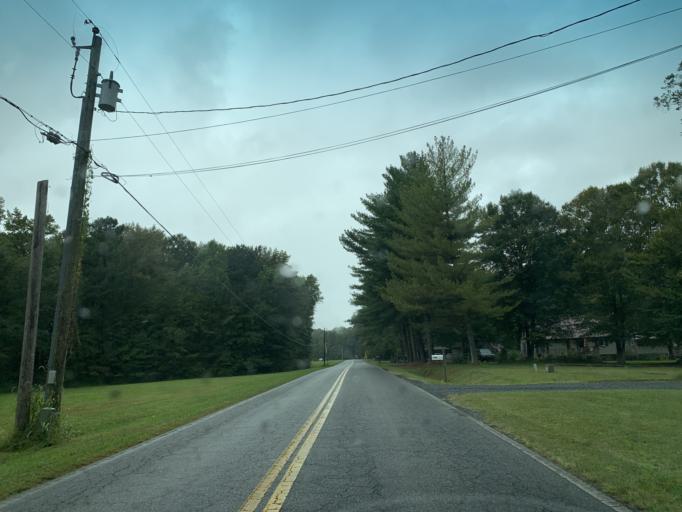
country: US
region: Maryland
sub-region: Caroline County
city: Denton
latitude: 38.9135
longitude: -75.8565
